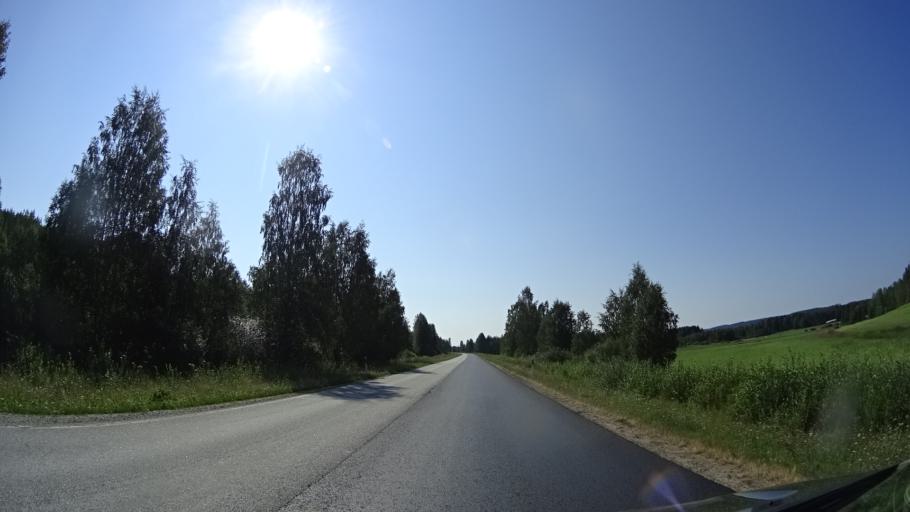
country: FI
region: North Karelia
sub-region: Joensuu
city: Juuka
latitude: 63.2159
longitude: 29.3035
